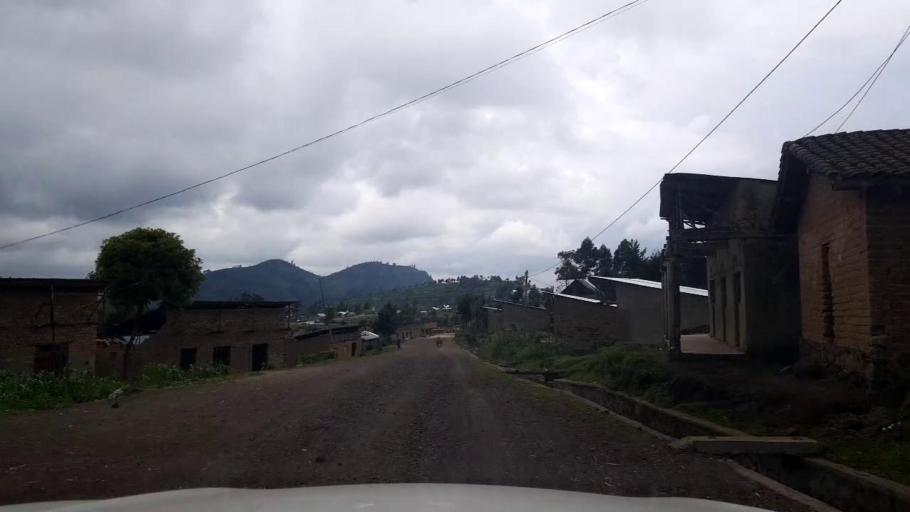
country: RW
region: Northern Province
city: Musanze
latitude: -1.5760
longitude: 29.4892
